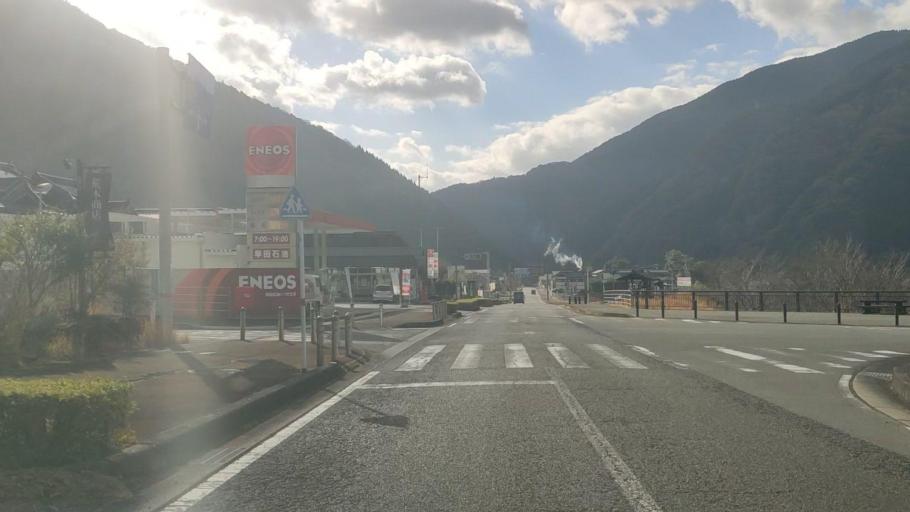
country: JP
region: Kumamoto
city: Hitoyoshi
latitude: 32.4002
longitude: 130.8265
